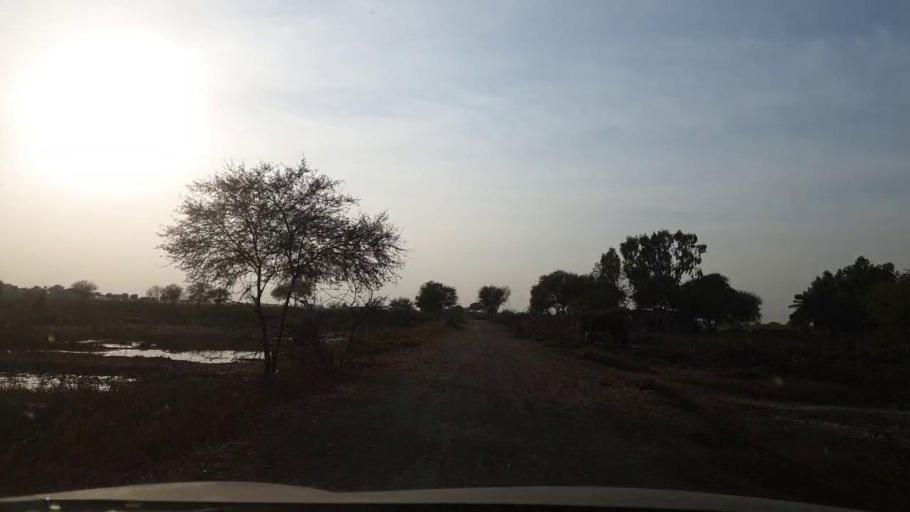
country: PK
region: Sindh
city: Berani
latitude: 25.7068
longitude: 68.7518
